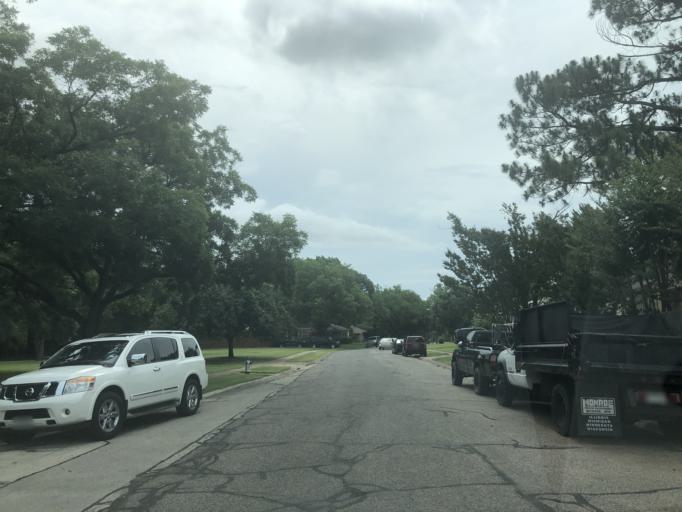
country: US
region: Texas
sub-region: Dallas County
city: Irving
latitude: 32.8029
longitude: -96.9498
